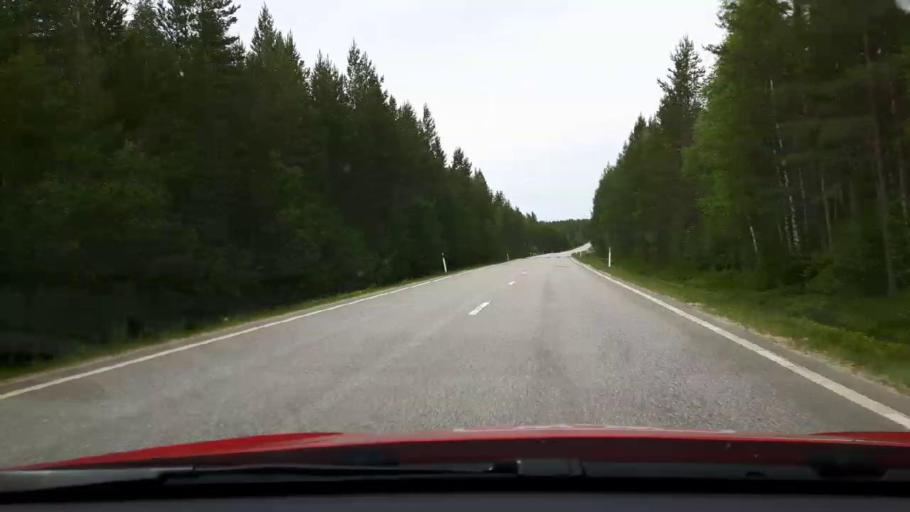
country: SE
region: Jaemtland
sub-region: Harjedalens Kommun
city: Sveg
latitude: 62.1086
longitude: 14.1929
